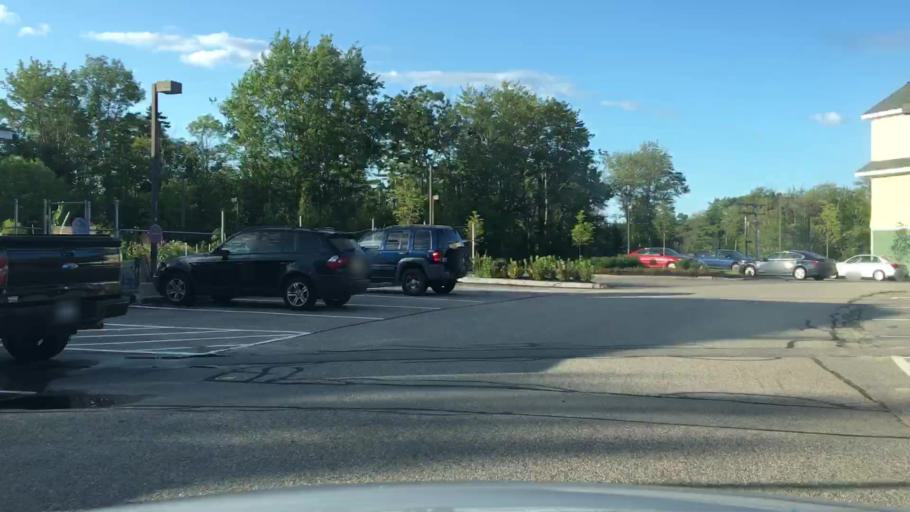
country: US
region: Maine
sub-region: Cumberland County
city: Scarborough
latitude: 43.5580
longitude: -70.2892
